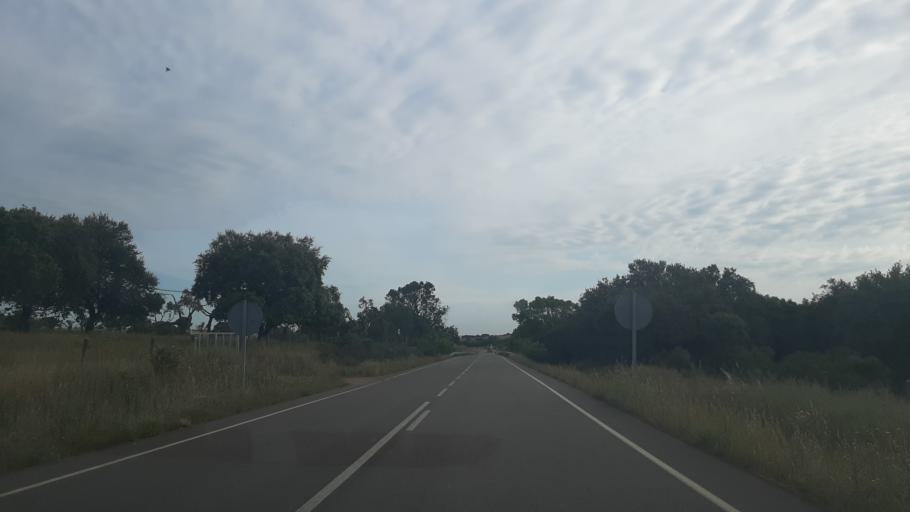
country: ES
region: Castille and Leon
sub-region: Provincia de Salamanca
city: Espeja
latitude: 40.5957
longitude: -6.7042
